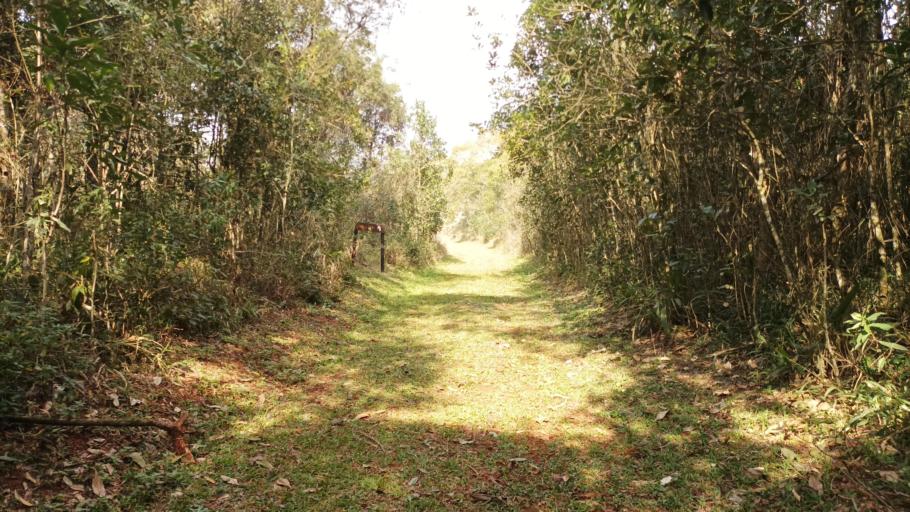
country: AR
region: Misiones
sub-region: Departamento de San Pedro
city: San Pedro
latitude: -26.6291
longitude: -54.1044
